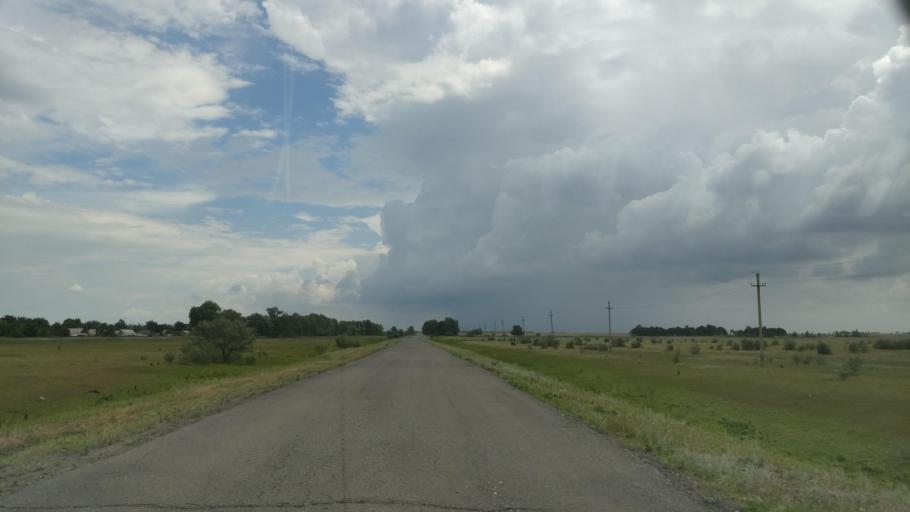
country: KZ
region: Pavlodar
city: Pavlodar
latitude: 52.6364
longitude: 77.3202
